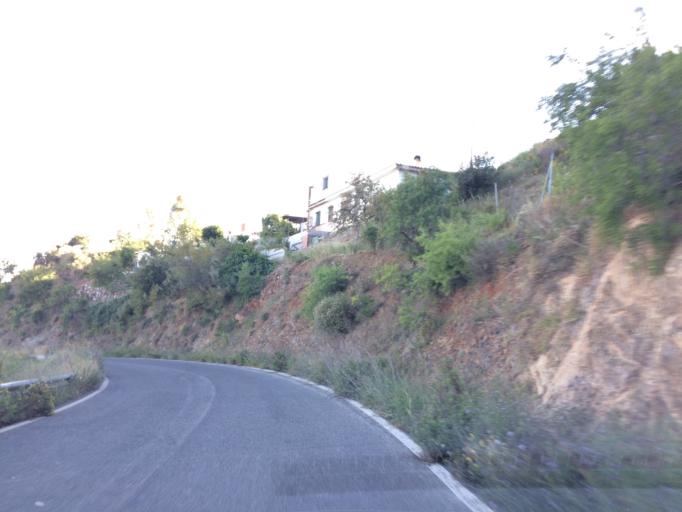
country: ES
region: Andalusia
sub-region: Provincia de Malaga
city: Totalan
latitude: 36.7567
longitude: -4.3299
